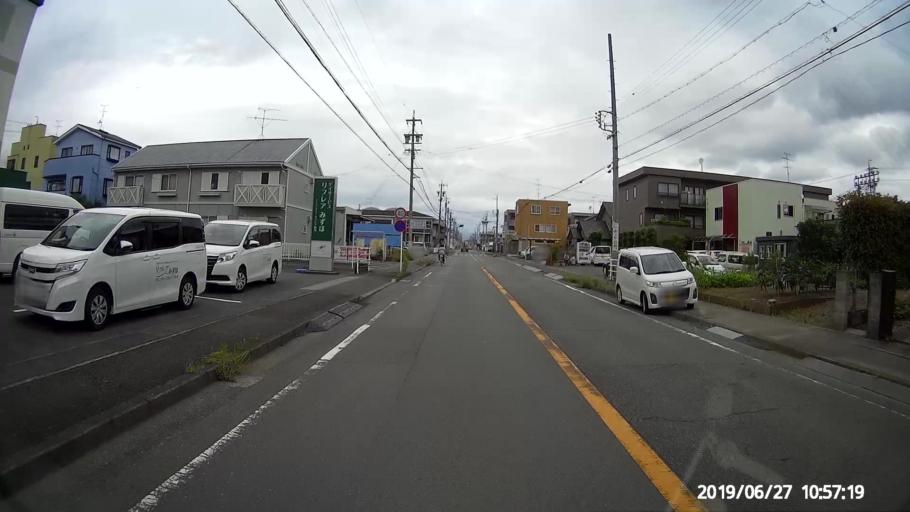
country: JP
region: Shizuoka
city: Shizuoka-shi
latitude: 34.9365
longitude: 138.3668
